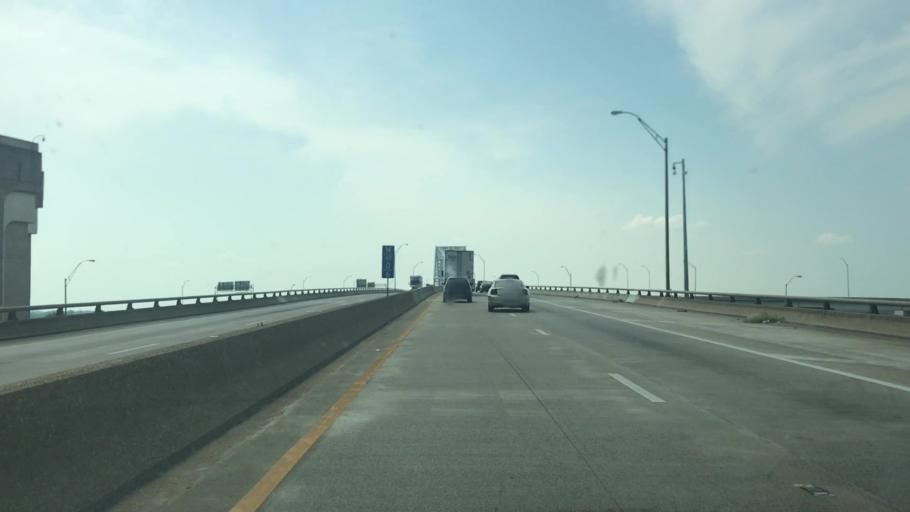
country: US
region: Tennessee
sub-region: Shelby County
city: Memphis
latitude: 35.1531
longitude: -90.0507
